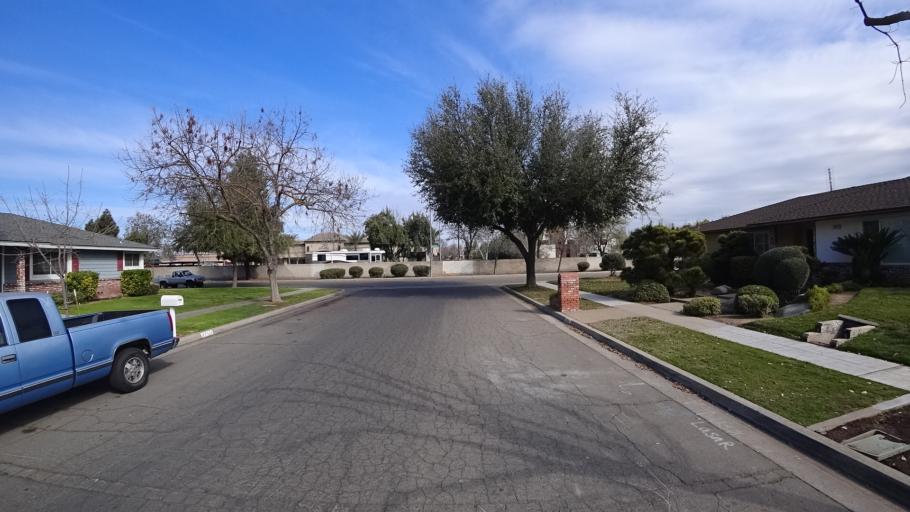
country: US
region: California
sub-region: Fresno County
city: Clovis
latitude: 36.8368
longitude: -119.7514
